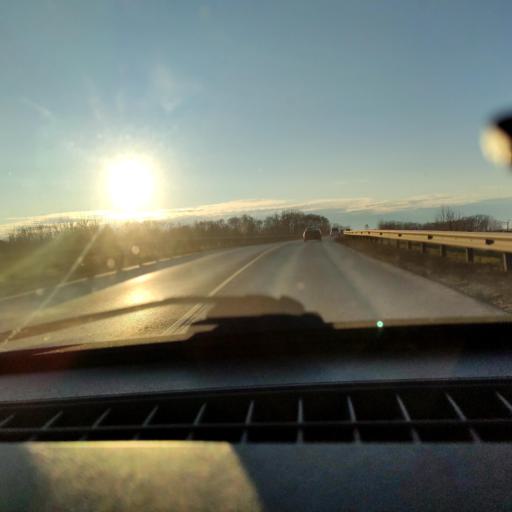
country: RU
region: Bashkortostan
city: Ufa
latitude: 54.6108
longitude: 55.8865
